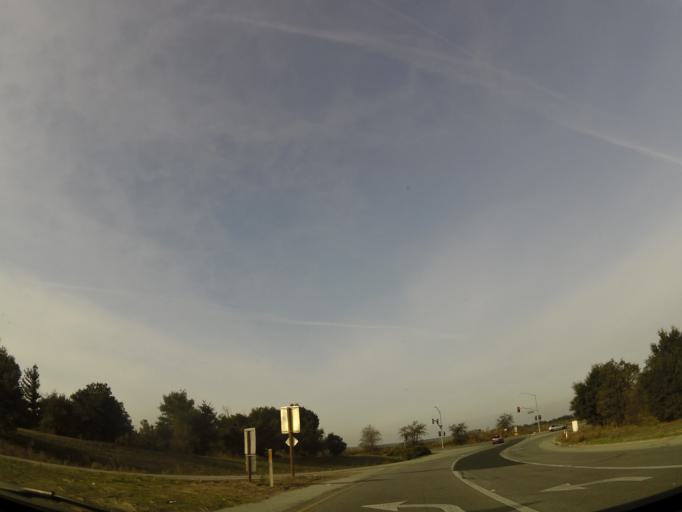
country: US
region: California
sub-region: San Benito County
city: Hollister
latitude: 36.8519
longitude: -121.4500
